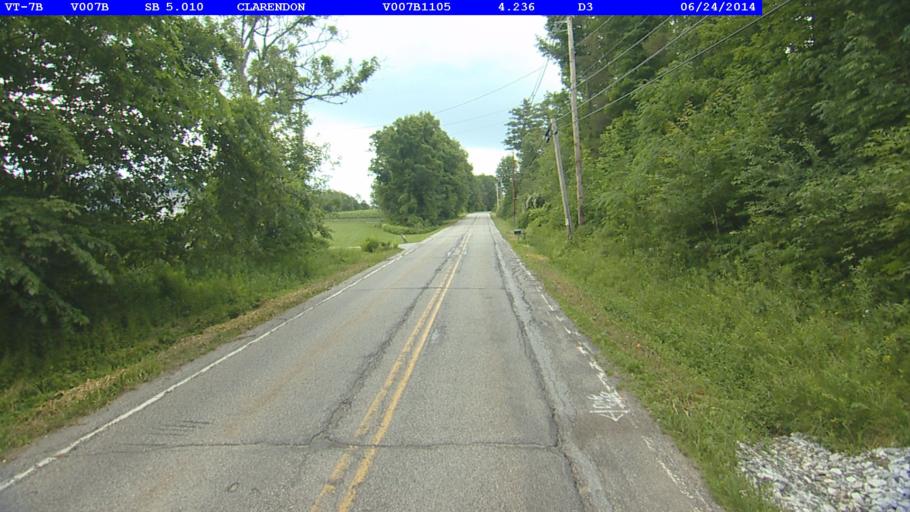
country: US
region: Vermont
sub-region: Rutland County
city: Rutland
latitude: 43.5585
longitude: -72.9626
